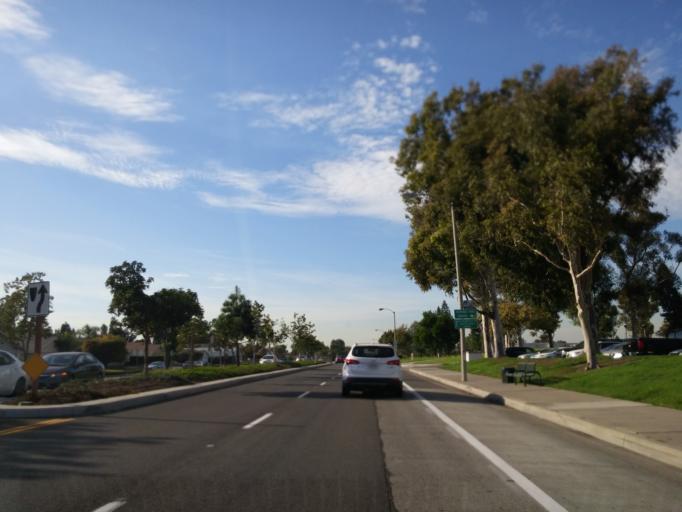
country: US
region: California
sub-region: Orange County
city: Irvine
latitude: 33.6987
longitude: -117.7788
